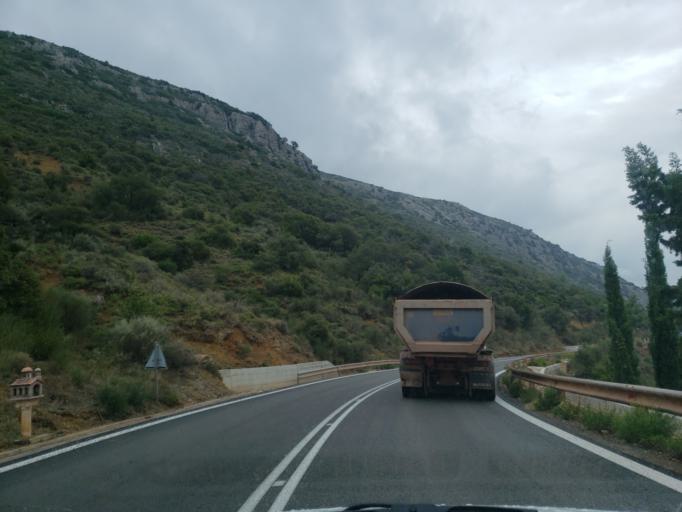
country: GR
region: Central Greece
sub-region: Nomos Fokidos
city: Amfissa
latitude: 38.5659
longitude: 22.4006
